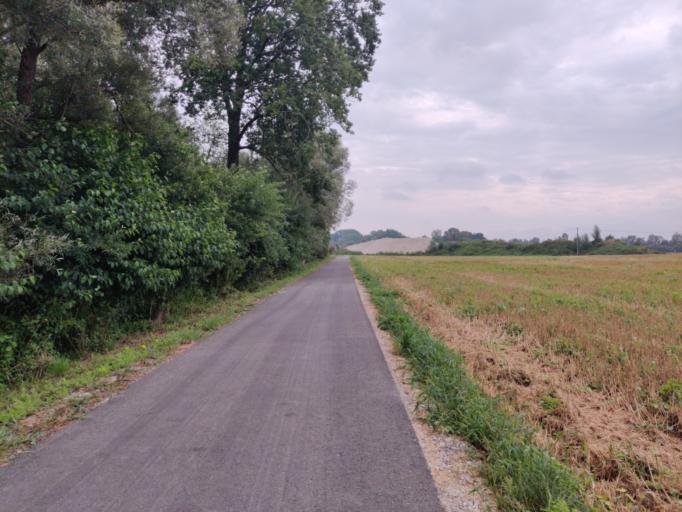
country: AT
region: Upper Austria
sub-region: Politischer Bezirk Linz-Land
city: Asten
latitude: 48.2323
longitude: 14.4477
